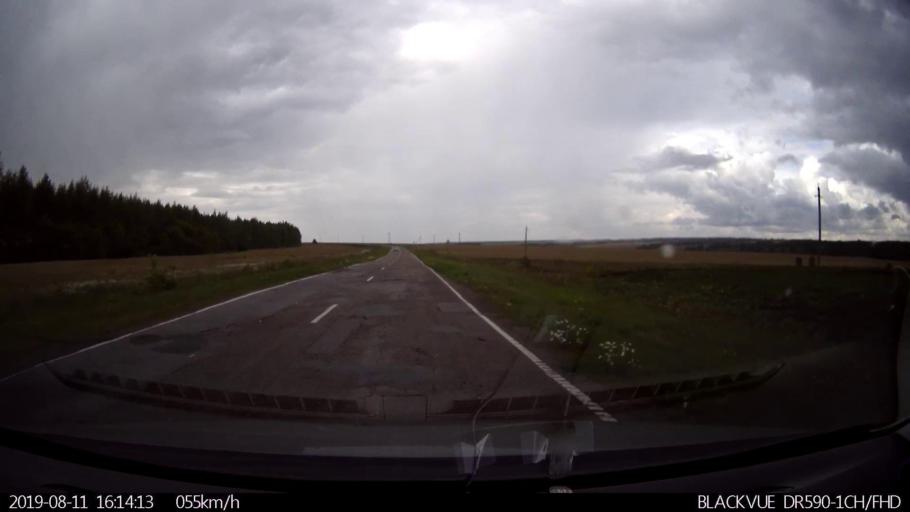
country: RU
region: Ulyanovsk
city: Ignatovka
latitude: 54.0263
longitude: 47.6346
